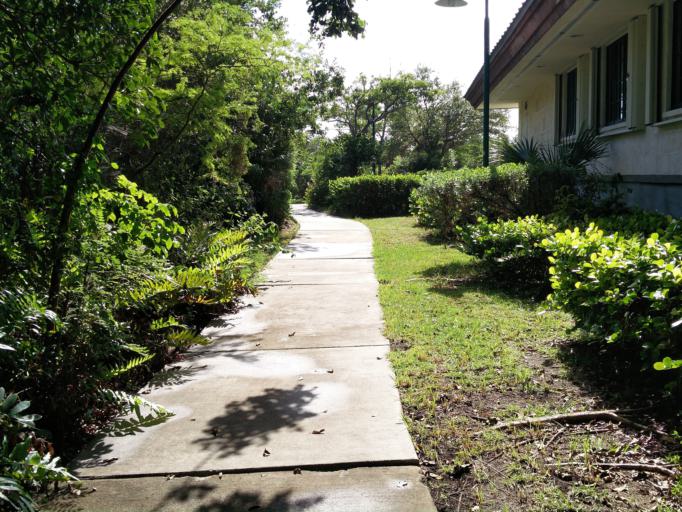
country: US
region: Florida
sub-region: Broward County
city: Dania Beach
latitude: 26.0383
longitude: -80.1194
